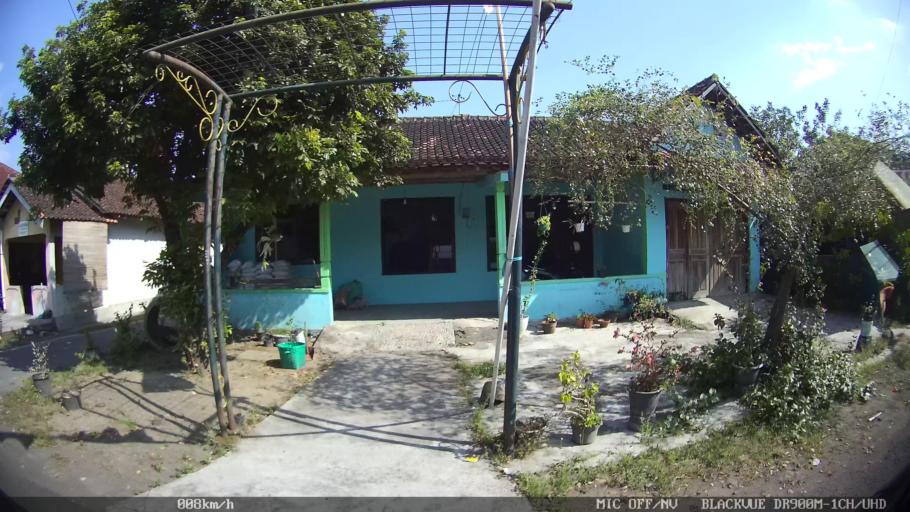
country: ID
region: Daerah Istimewa Yogyakarta
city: Yogyakarta
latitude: -7.8281
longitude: 110.3921
